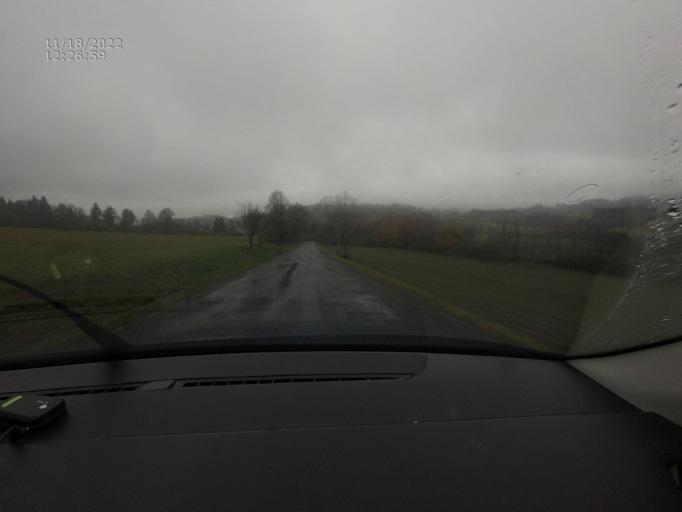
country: CZ
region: Plzensky
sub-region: Okres Klatovy
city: Planice
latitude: 49.4302
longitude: 13.5053
